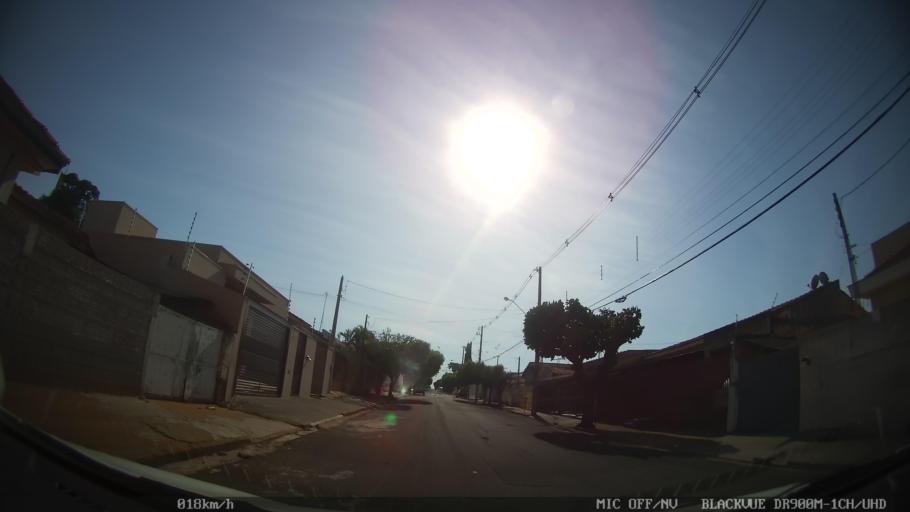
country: BR
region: Sao Paulo
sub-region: Sao Jose Do Rio Preto
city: Sao Jose do Rio Preto
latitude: -20.8007
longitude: -49.3835
